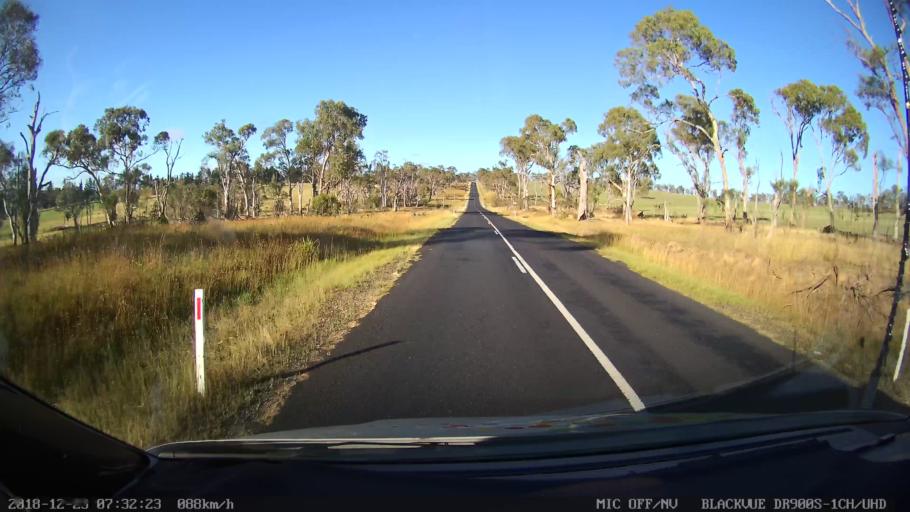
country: AU
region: New South Wales
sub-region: Armidale Dumaresq
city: Enmore
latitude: -30.5044
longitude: 152.1178
